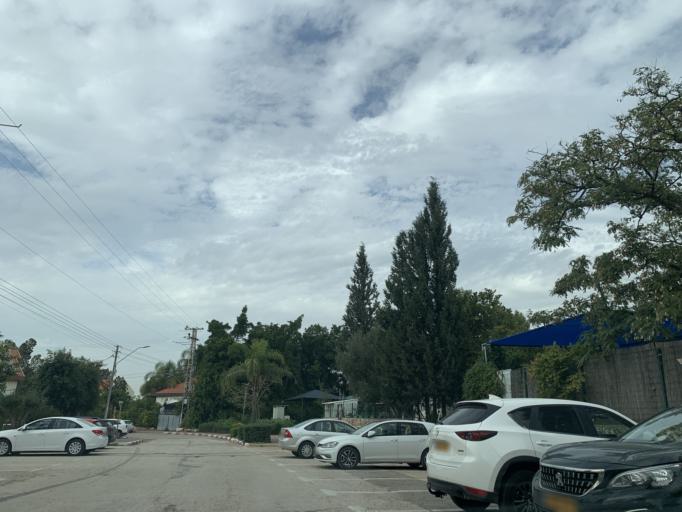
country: IL
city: Nirit
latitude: 32.1459
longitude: 34.9858
